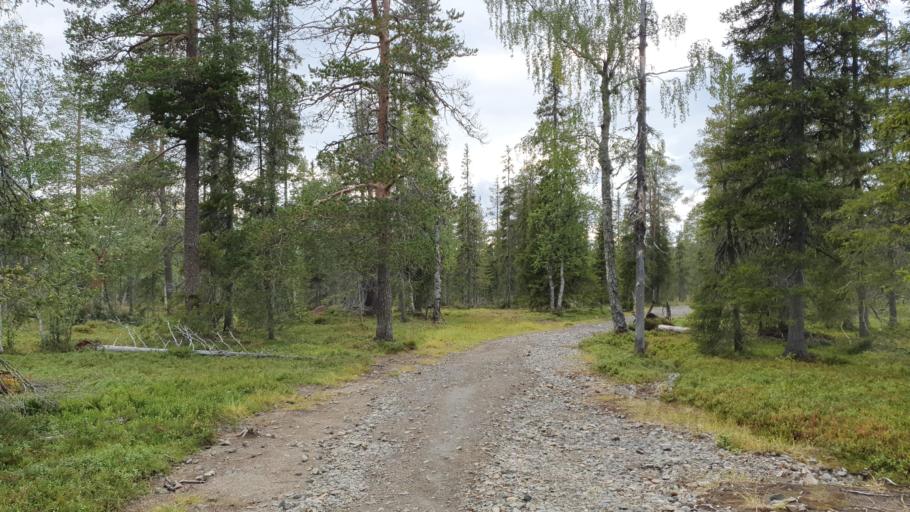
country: FI
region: Lapland
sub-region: Tunturi-Lappi
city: Kolari
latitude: 67.6180
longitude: 24.2334
